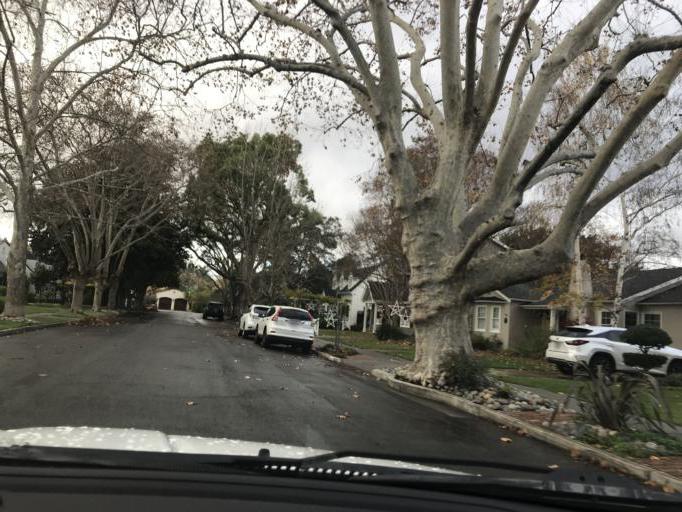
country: US
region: California
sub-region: Santa Clara County
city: Buena Vista
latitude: 37.2959
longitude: -121.9062
